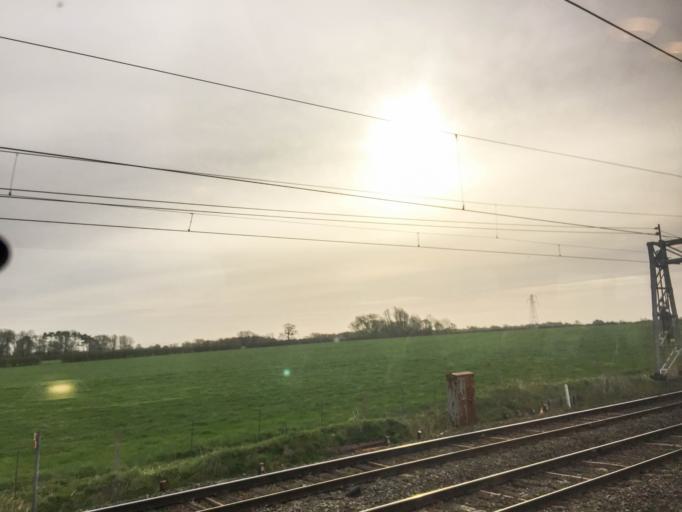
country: GB
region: England
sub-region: Cheshire West and Chester
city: Winsford
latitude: 53.1716
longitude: -2.4801
